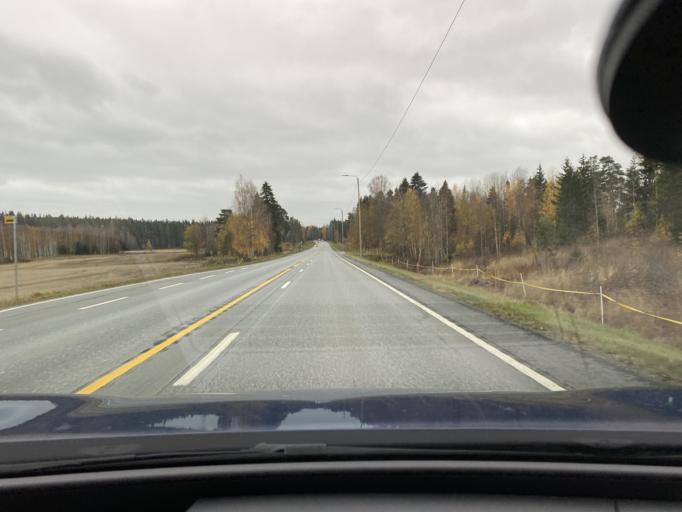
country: FI
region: Varsinais-Suomi
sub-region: Vakka-Suomi
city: Laitila
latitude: 60.9413
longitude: 21.6021
